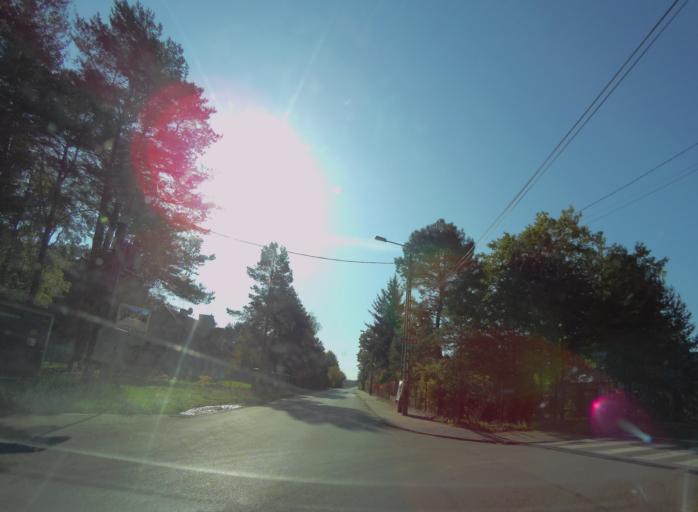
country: PL
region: Masovian Voivodeship
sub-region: Powiat otwocki
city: Jozefow
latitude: 52.1690
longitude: 21.3021
